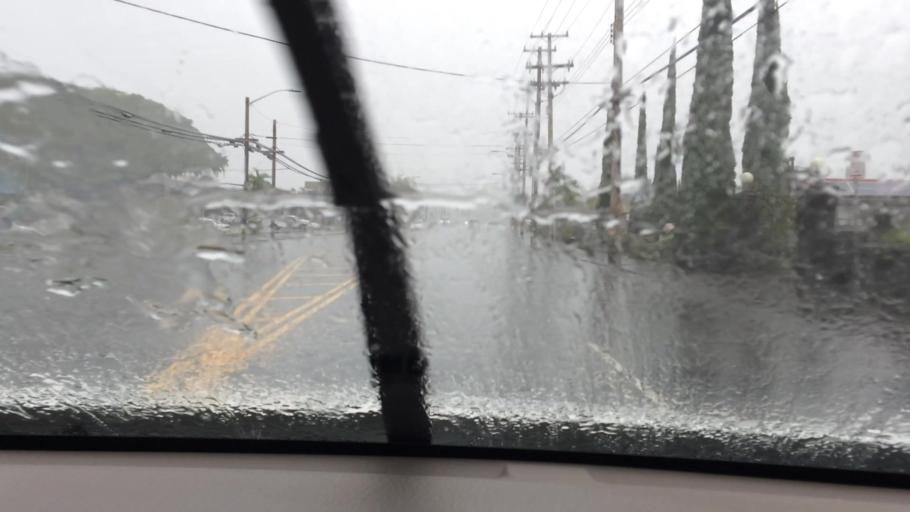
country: US
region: Hawaii
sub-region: Hawaii County
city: Hilo
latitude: 19.7203
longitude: -155.0831
